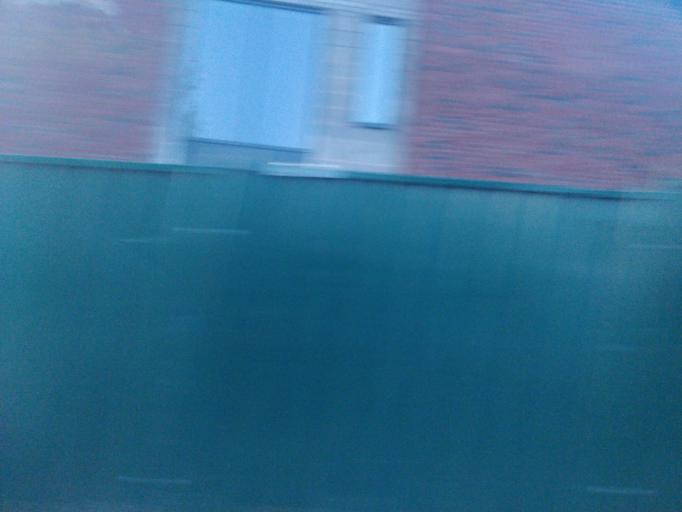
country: GB
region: England
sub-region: Lancashire
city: Tarleton
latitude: 53.7004
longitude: -2.8028
